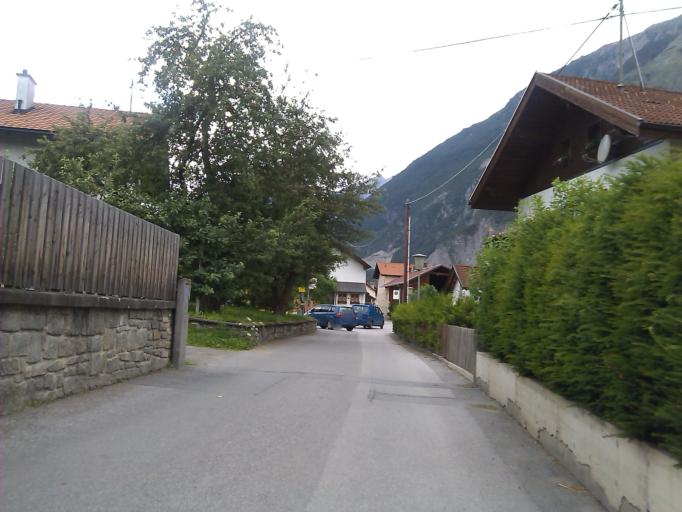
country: AT
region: Tyrol
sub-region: Politischer Bezirk Imst
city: Mils bei Imst
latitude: 47.2010
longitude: 10.6718
